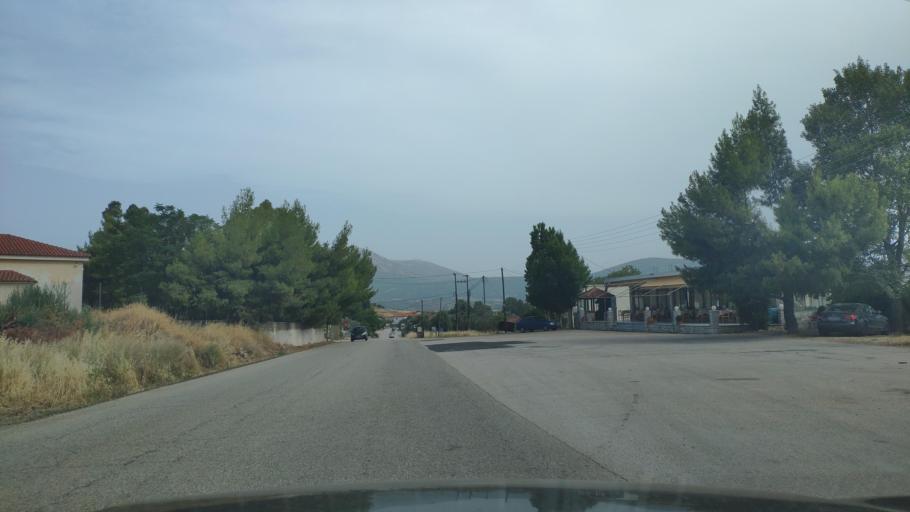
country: GR
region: Peloponnese
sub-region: Nomos Argolidos
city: Palaia Epidavros
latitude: 37.5648
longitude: 23.1505
